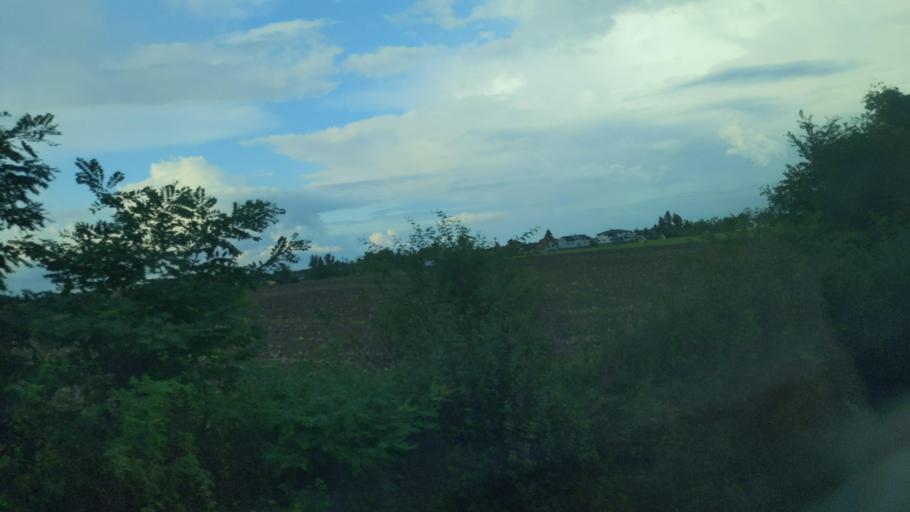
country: CZ
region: Central Bohemia
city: Uvaly
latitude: 50.0769
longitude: 14.7658
